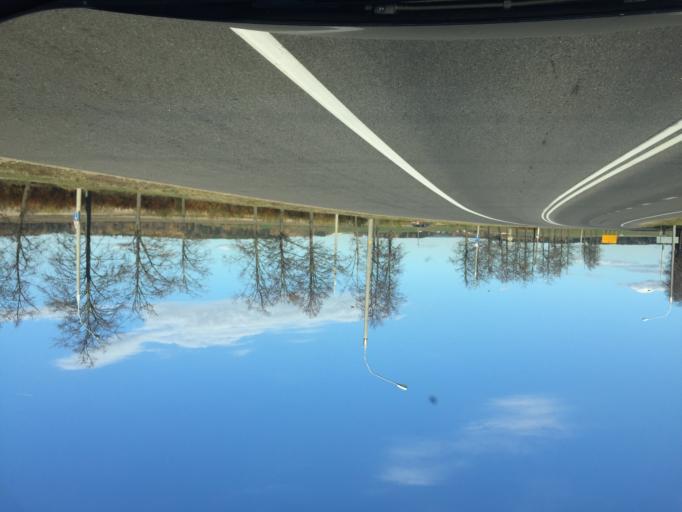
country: BY
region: Minsk
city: Slabada
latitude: 54.0206
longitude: 27.8881
